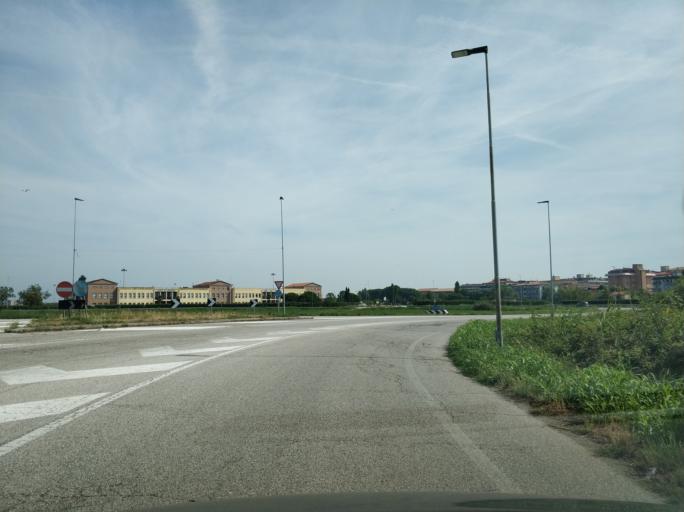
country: IT
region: Veneto
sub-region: Provincia di Venezia
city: Chioggia
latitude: 45.2017
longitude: 12.2716
